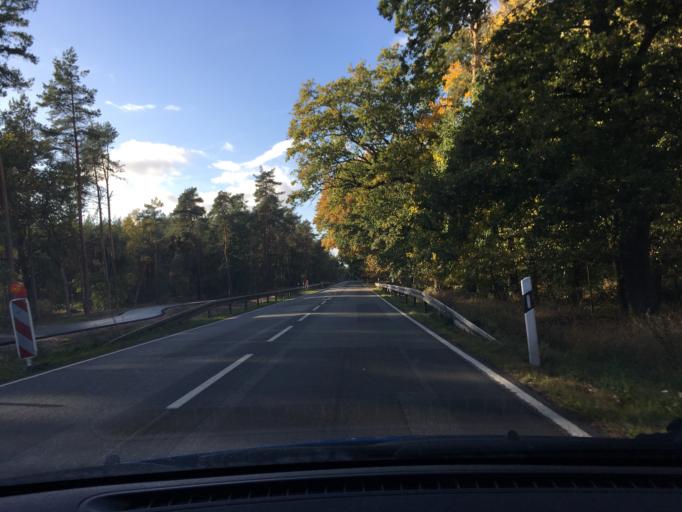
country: DE
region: Mecklenburg-Vorpommern
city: Boizenburg
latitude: 53.3896
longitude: 10.8268
